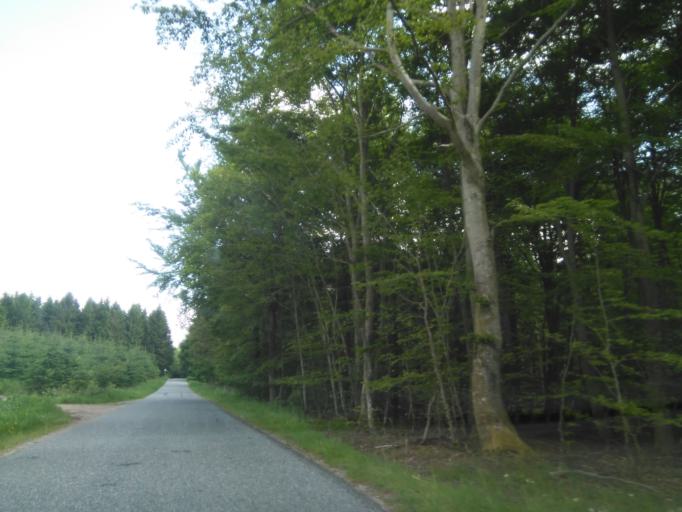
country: DK
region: Central Jutland
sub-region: Skanderborg Kommune
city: Galten
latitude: 56.2246
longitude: 9.9272
